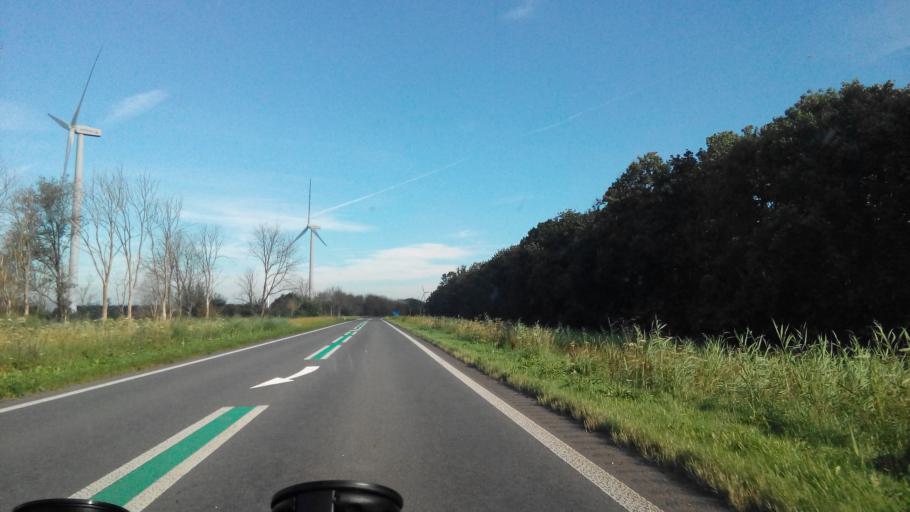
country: NL
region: Utrecht
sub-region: Gemeente Bunschoten
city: Bunschoten
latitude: 52.3151
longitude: 5.4399
